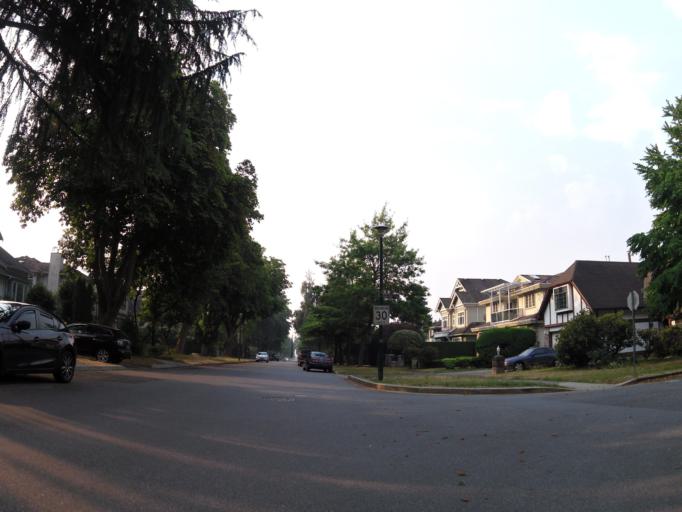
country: CA
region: British Columbia
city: Vancouver
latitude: 49.2259
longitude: -123.1481
